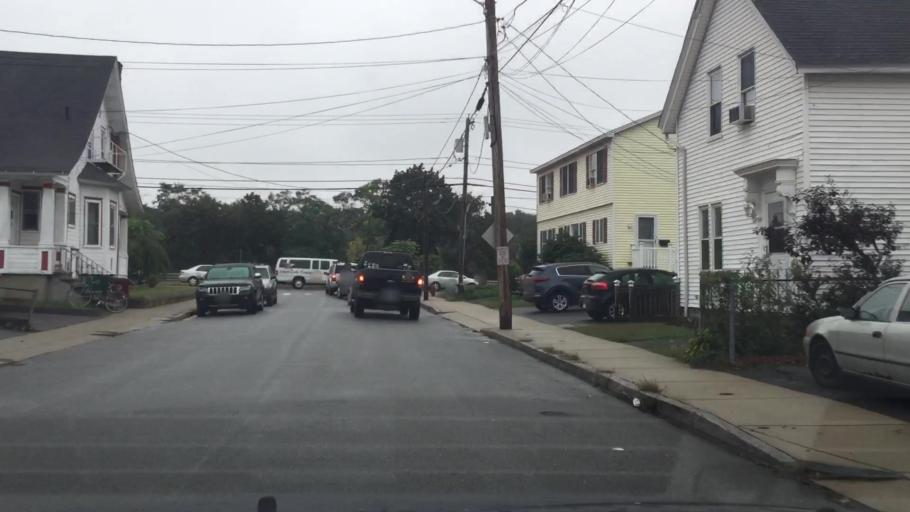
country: US
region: Massachusetts
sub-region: Middlesex County
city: Lowell
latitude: 42.6519
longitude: -71.3305
